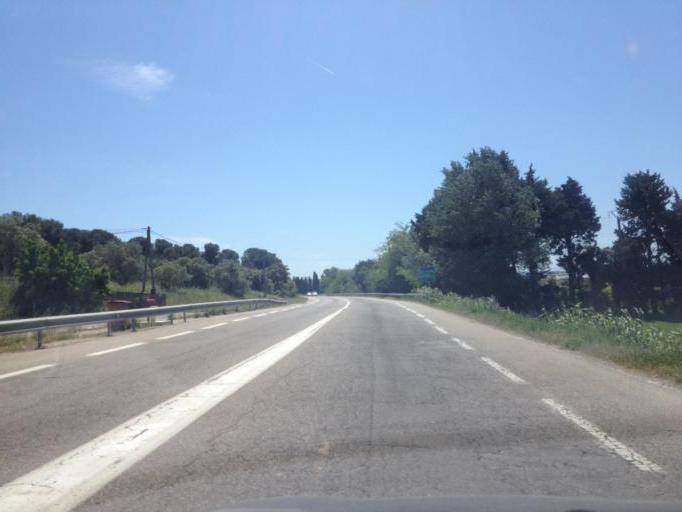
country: FR
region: Provence-Alpes-Cote d'Azur
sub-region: Departement du Vaucluse
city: Cavaillon
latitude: 43.8452
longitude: 5.0167
